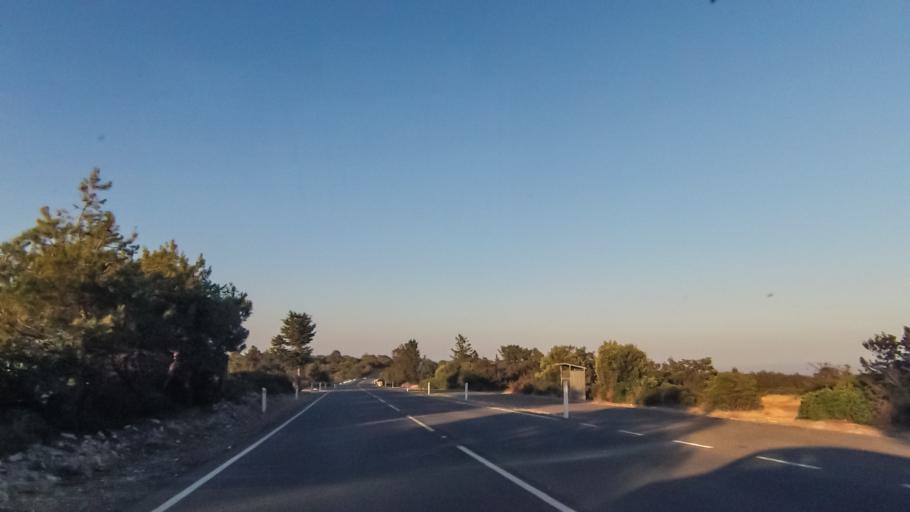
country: CY
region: Limassol
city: Sotira
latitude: 34.6699
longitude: 32.8660
